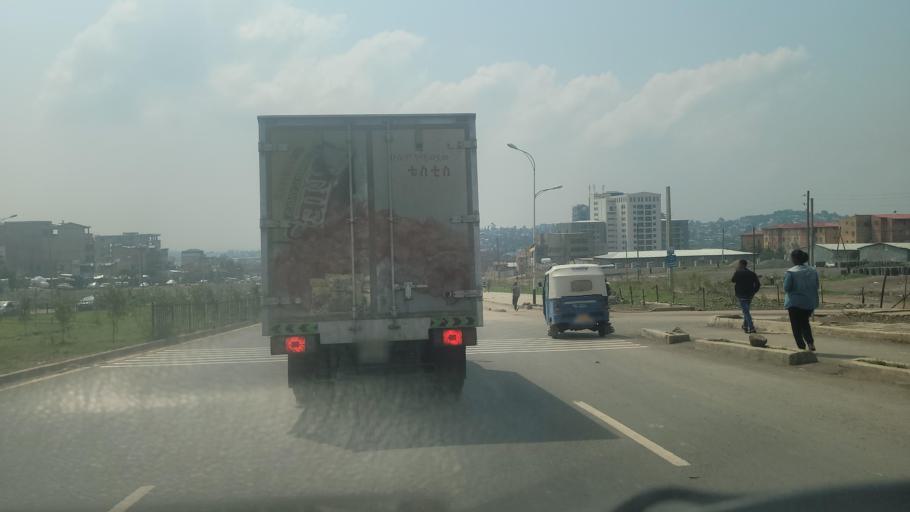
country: ET
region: Adis Abeba
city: Addis Ababa
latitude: 8.9377
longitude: 38.7295
